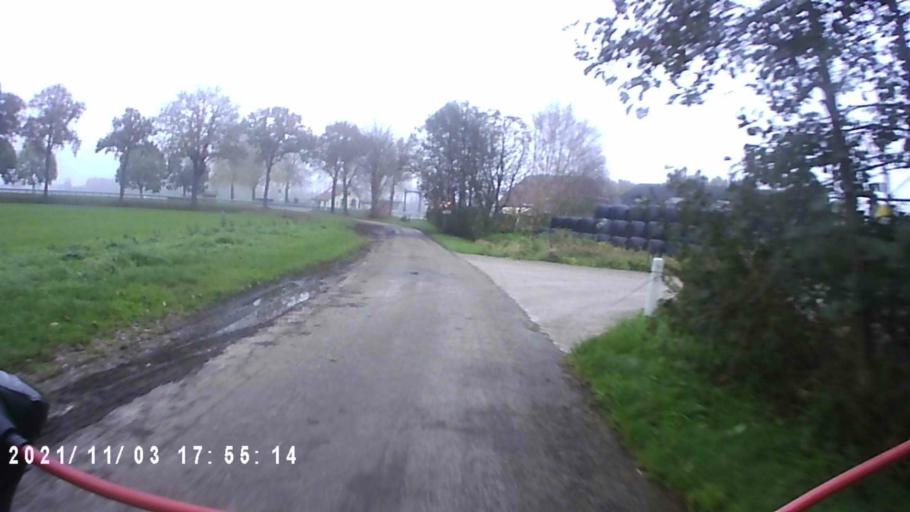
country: NL
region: Drenthe
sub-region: Gemeente Westerveld
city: Dwingeloo
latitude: 52.8393
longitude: 6.3315
